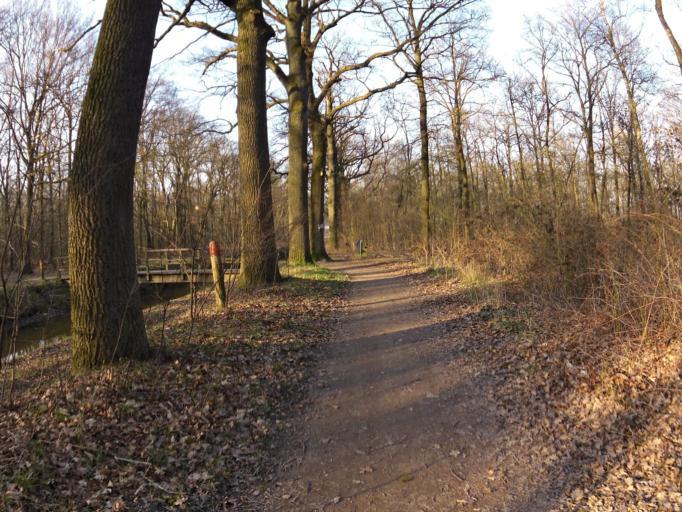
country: NL
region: North Brabant
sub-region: Gemeente Maasdonk
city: Geffen
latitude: 51.7061
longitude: 5.4007
